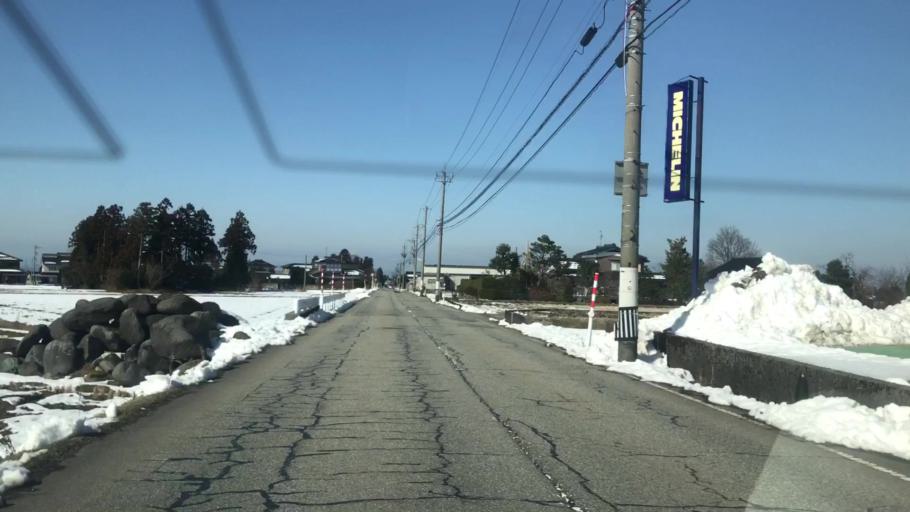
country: JP
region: Toyama
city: Toyama-shi
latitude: 36.6185
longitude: 137.2865
